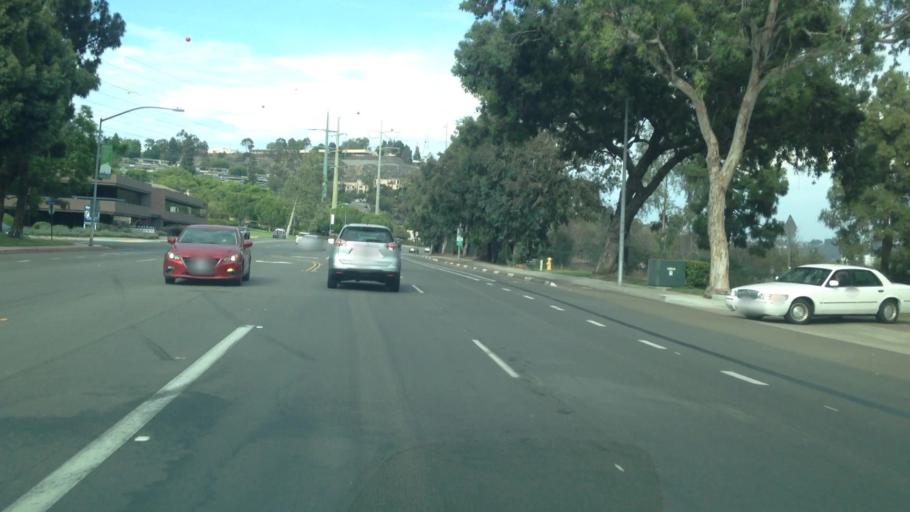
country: US
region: California
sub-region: San Diego County
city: San Diego
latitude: 32.7655
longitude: -117.1876
